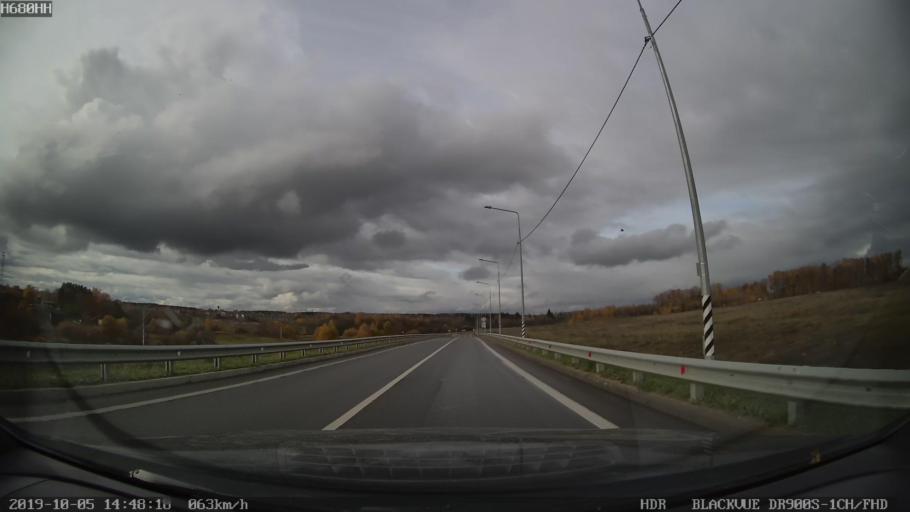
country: RU
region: Moskovskaya
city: Solnechnogorsk
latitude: 56.2147
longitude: 36.9012
